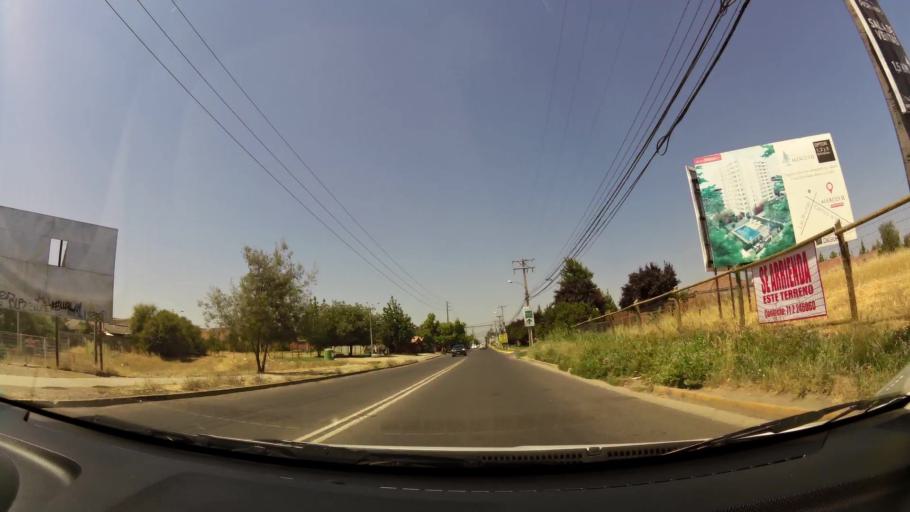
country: CL
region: Maule
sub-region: Provincia de Talca
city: Talca
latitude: -35.4320
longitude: -71.6265
